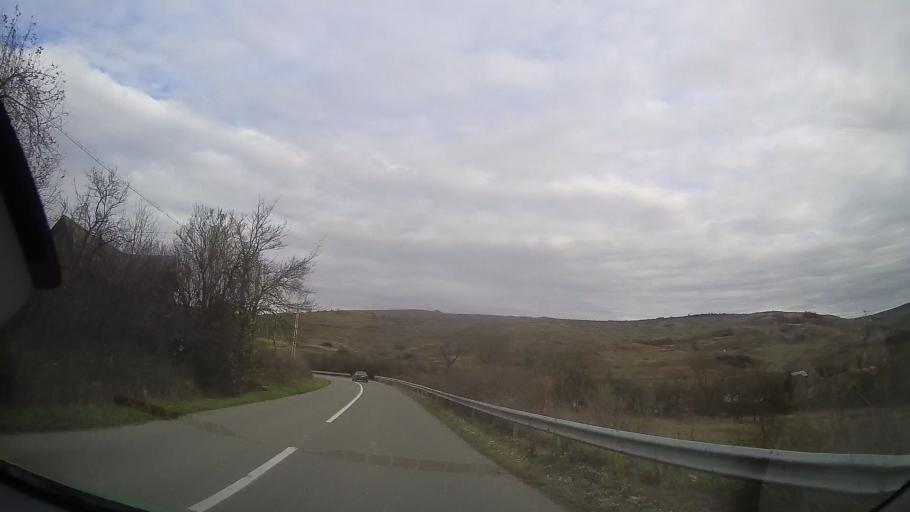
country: RO
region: Bistrita-Nasaud
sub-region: Comuna Milas
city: Milas
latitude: 46.8355
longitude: 24.4481
